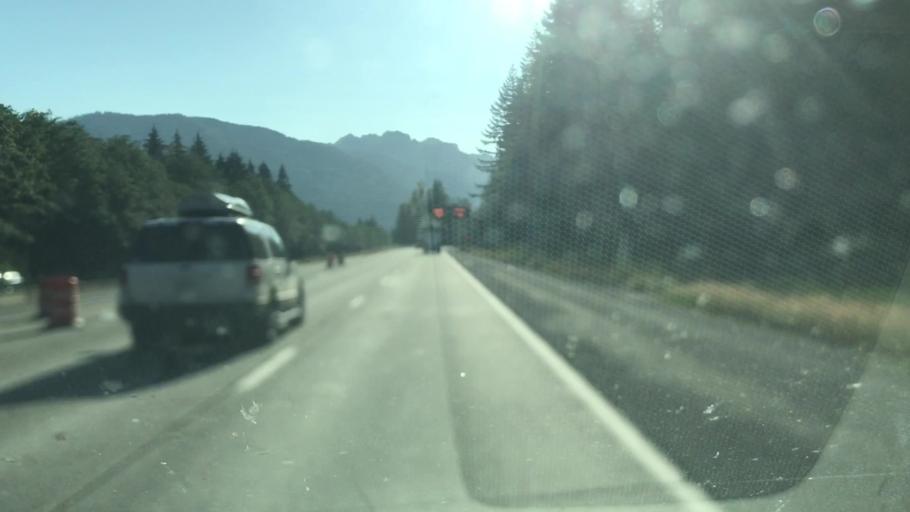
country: US
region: Washington
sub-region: King County
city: Tanner
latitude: 47.3967
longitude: -121.4998
